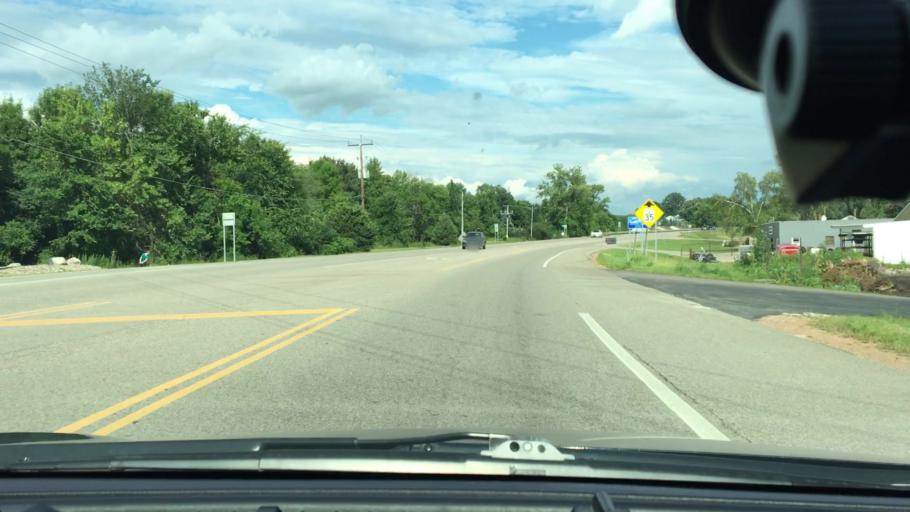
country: US
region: Minnesota
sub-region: Carver County
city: Victoria
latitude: 44.8614
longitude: -93.6712
